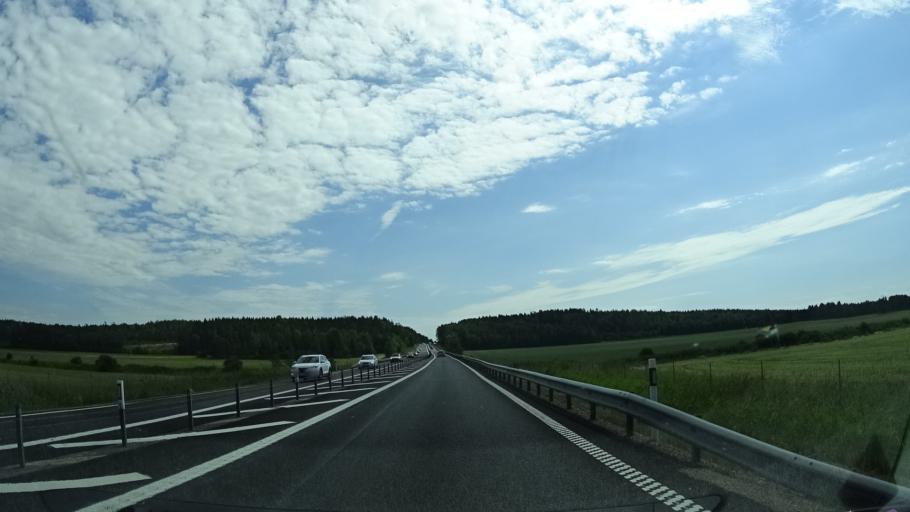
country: SE
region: Vaermland
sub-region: Karlstads Kommun
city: Skattkarr
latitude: 59.4024
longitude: 13.7837
